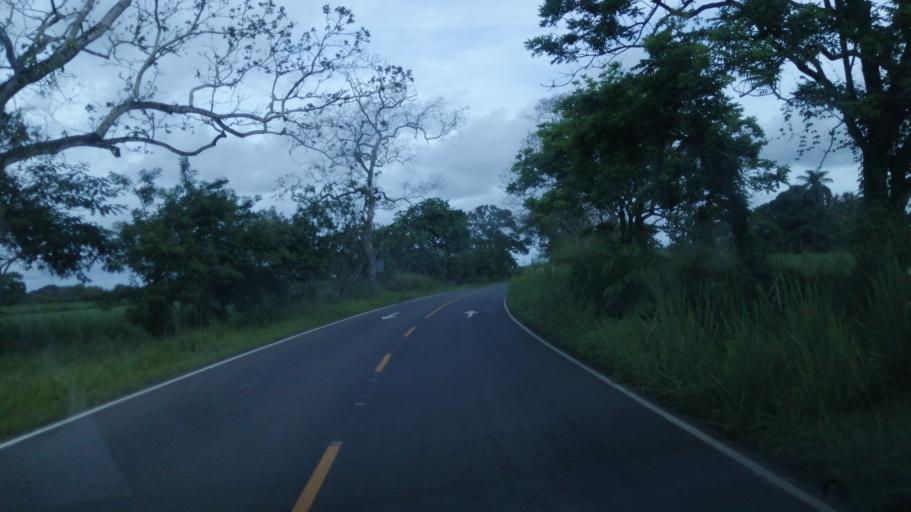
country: PA
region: Chiriqui
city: Alanje
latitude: 8.4076
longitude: -82.5136
